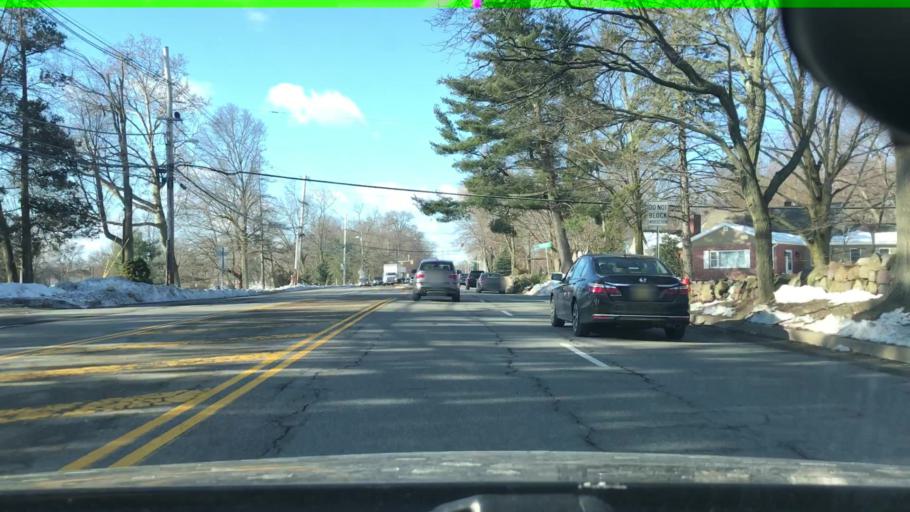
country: US
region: New Jersey
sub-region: Morris County
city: Parsippany
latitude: 40.8483
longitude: -74.4589
